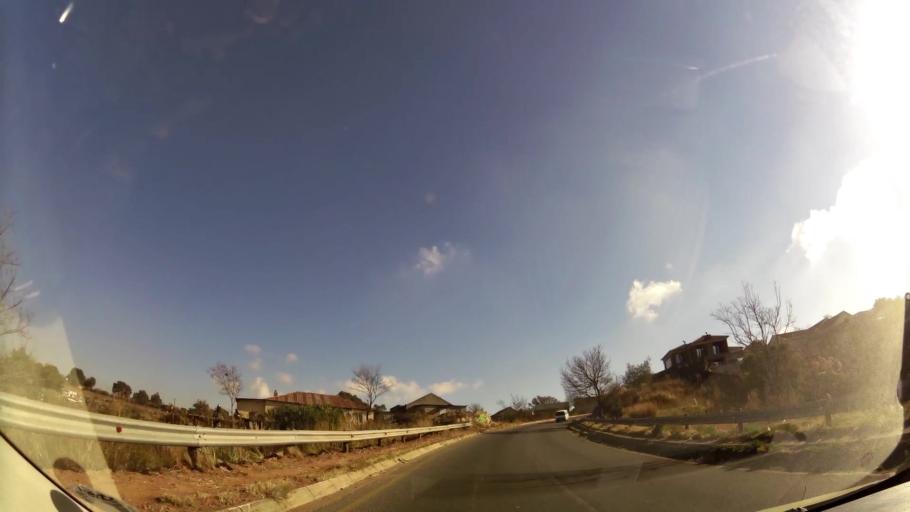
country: ZA
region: Gauteng
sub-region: City of Johannesburg Metropolitan Municipality
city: Roodepoort
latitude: -26.1520
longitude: 27.8406
